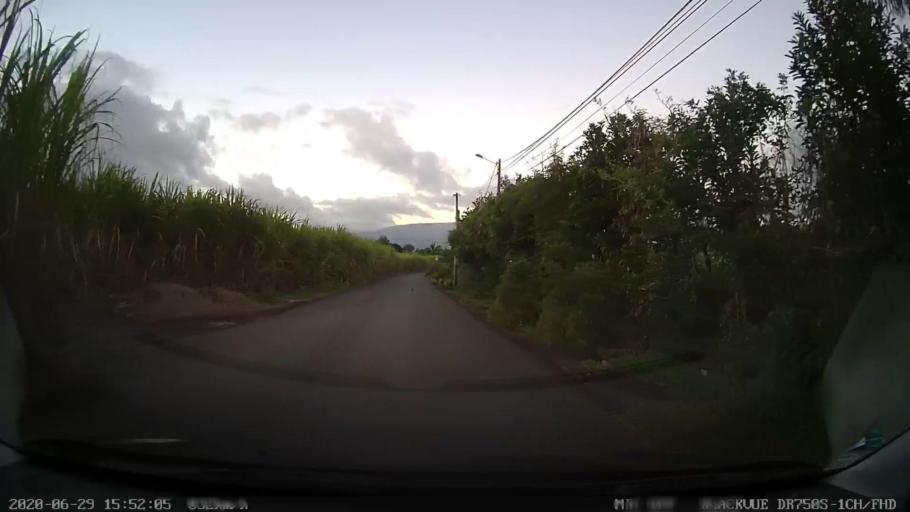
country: RE
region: Reunion
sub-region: Reunion
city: Bras-Panon
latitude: -20.9961
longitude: 55.6939
